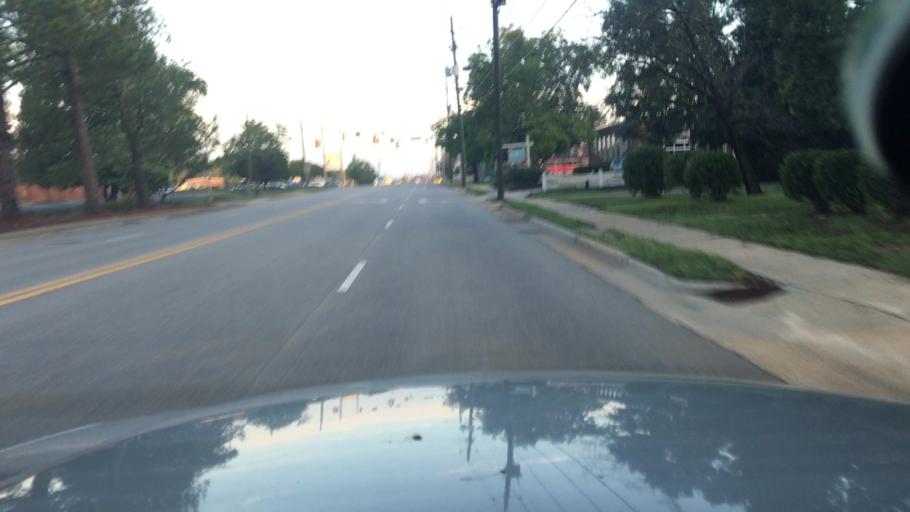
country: US
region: North Carolina
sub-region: Cumberland County
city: Fayetteville
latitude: 35.0704
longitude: -78.9229
